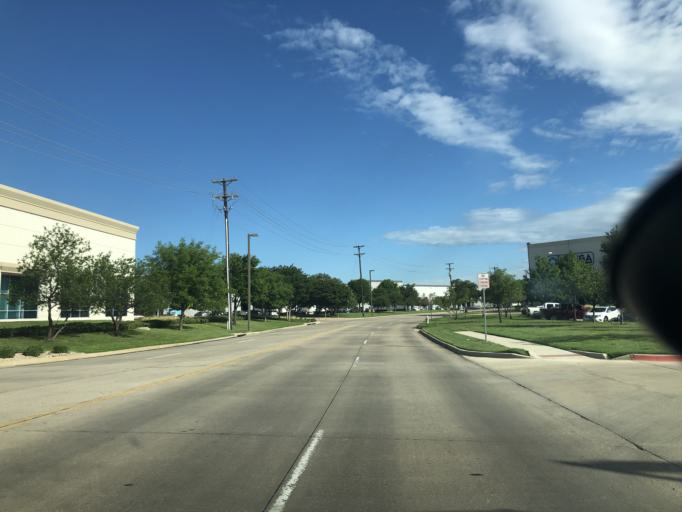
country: US
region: Texas
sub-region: Tarrant County
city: Euless
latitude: 32.8293
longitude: -97.0293
